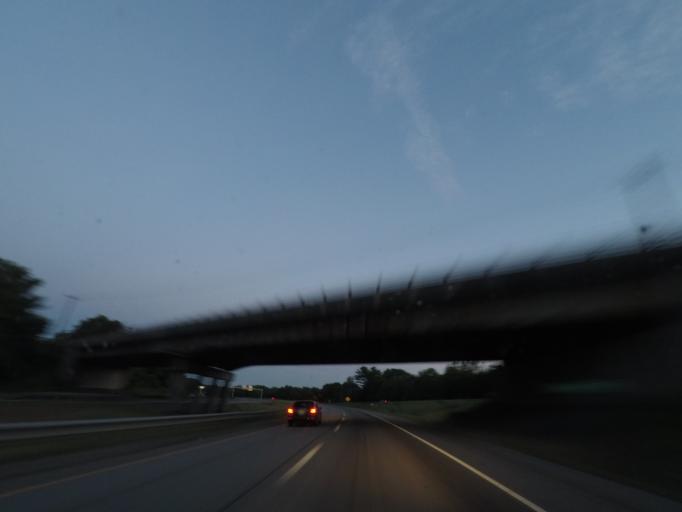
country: US
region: Connecticut
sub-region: Windham County
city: Putnam
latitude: 41.8999
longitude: -71.8992
